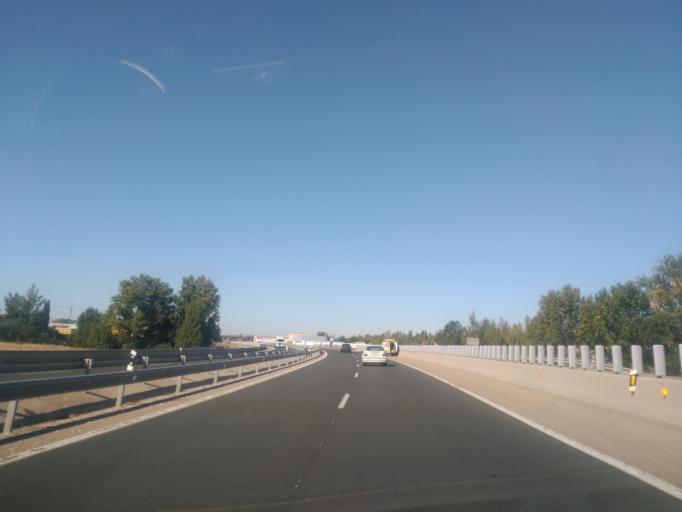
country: ES
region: Castille and Leon
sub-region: Provincia de Valladolid
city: Tudela de Duero
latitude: 41.5943
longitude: -4.5807
